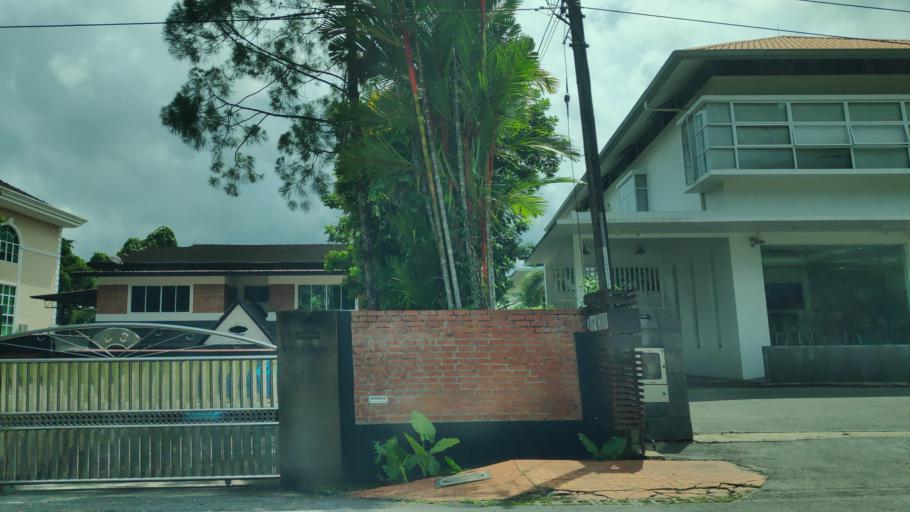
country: MY
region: Sarawak
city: Kuching
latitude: 1.5460
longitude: 110.3462
